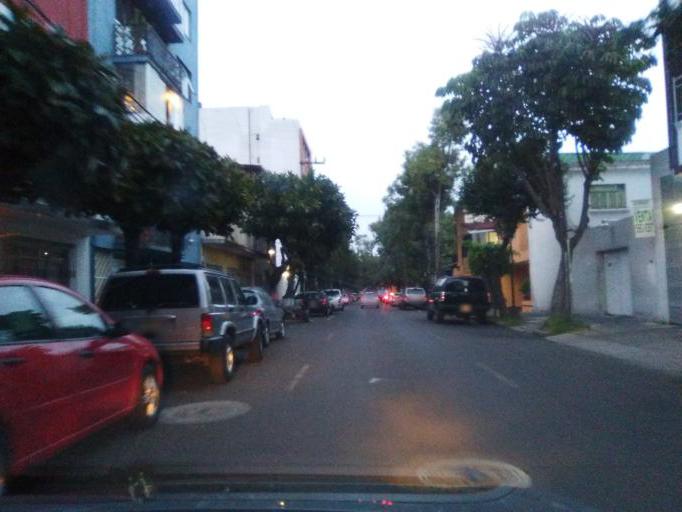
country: MX
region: Mexico City
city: Alvaro Obregon
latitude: 19.3768
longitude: -99.1908
